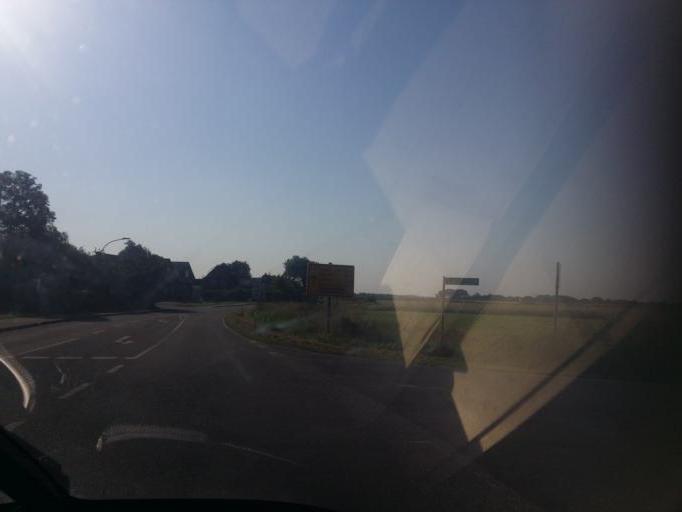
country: DE
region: Schleswig-Holstein
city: Neukirchen
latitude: 54.8954
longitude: 8.7502
